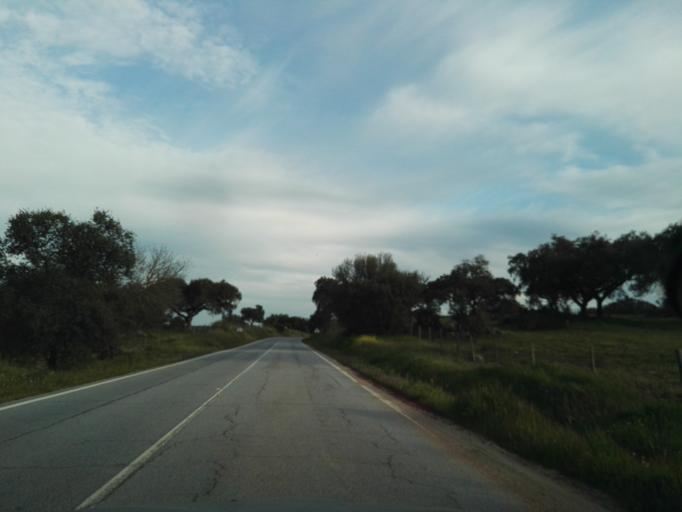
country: PT
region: Portalegre
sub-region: Arronches
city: Arronches
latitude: 39.0645
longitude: -7.2751
